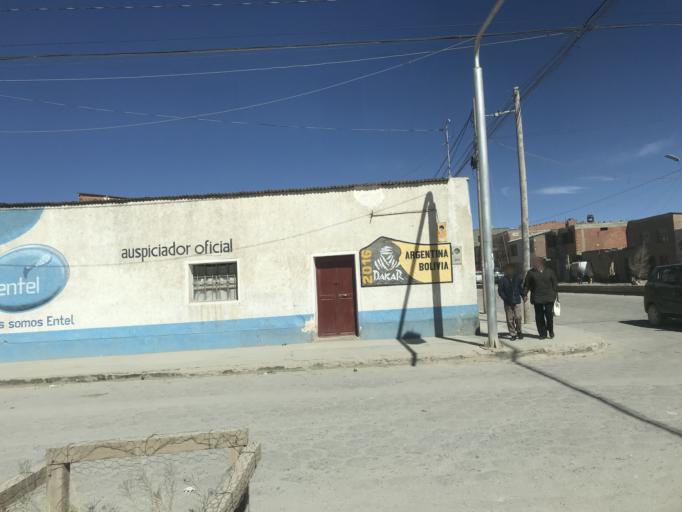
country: BO
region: Potosi
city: Uyuni
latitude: -20.4590
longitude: -66.8250
